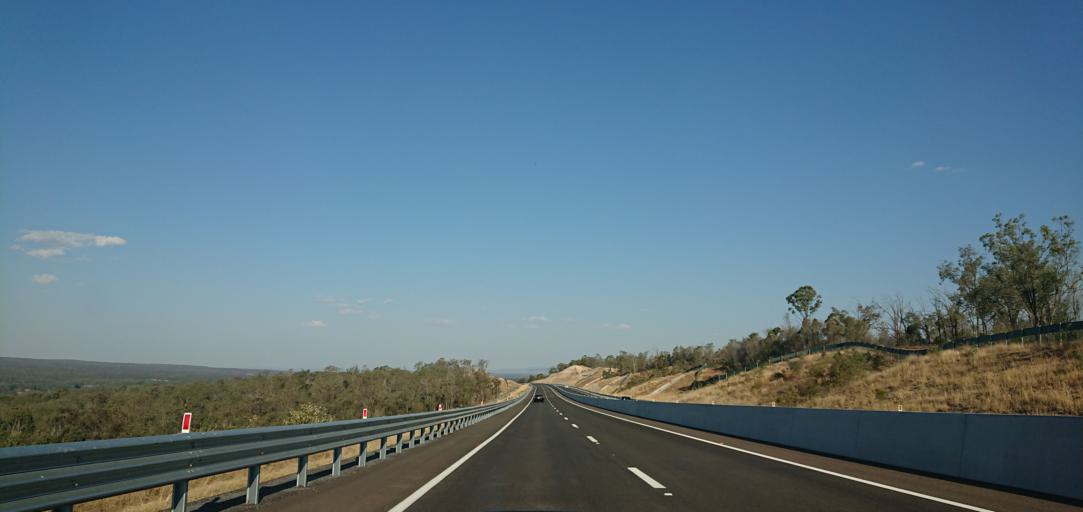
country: AU
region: Queensland
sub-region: Toowoomba
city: East Toowoomba
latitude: -27.5167
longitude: 152.0491
